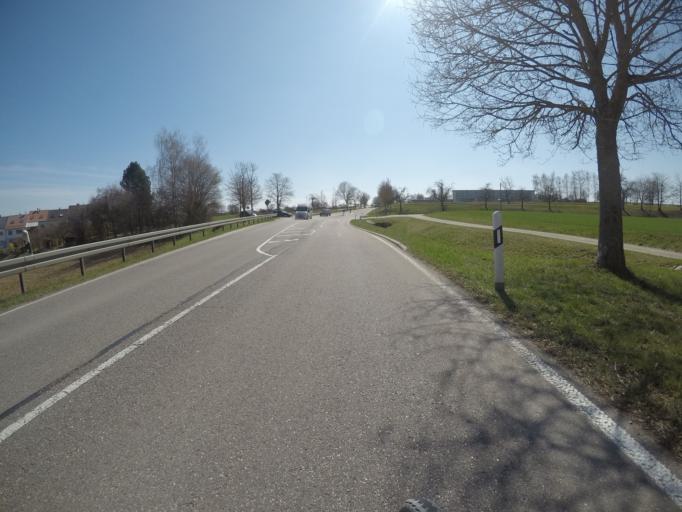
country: DE
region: Baden-Wuerttemberg
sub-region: Regierungsbezirk Stuttgart
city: Herrenberg
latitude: 48.5854
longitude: 8.8297
